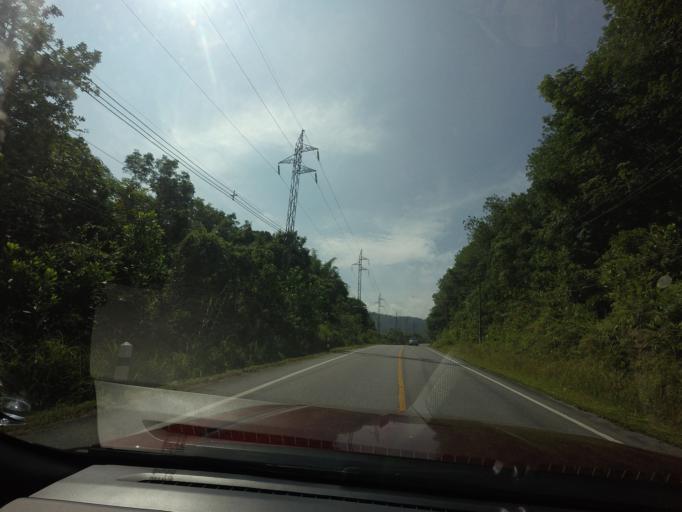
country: TH
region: Yala
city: Betong
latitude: 5.8432
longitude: 101.1148
